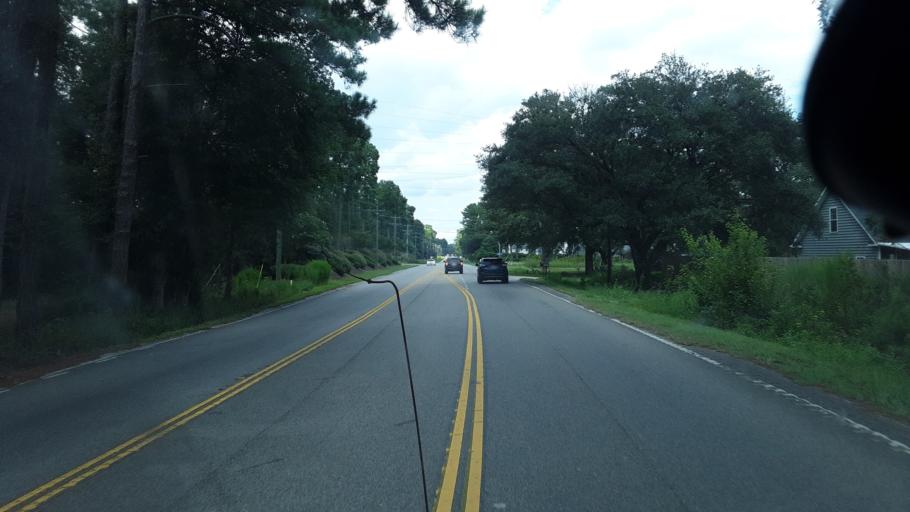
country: US
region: South Carolina
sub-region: Horry County
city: Forestbrook
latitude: 33.8222
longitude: -78.9024
